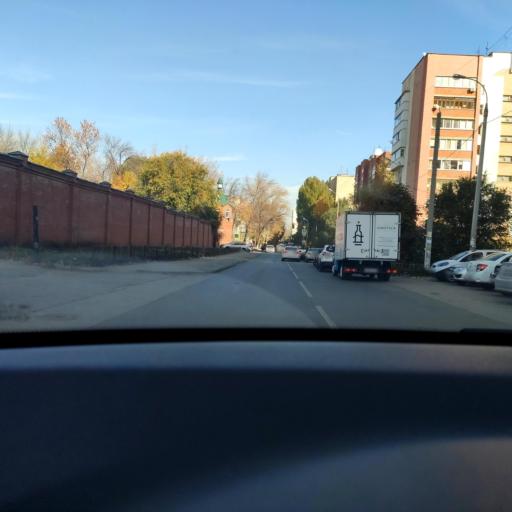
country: RU
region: Samara
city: Samara
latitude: 53.2310
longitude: 50.2456
